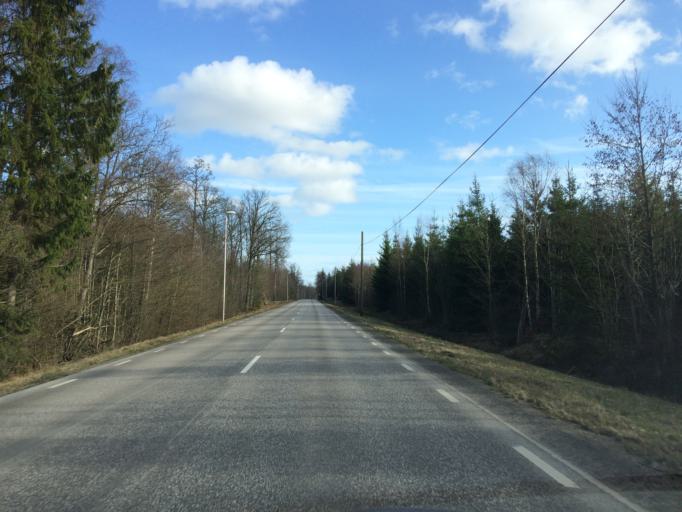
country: SE
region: Kronoberg
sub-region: Almhults Kommun
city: AElmhult
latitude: 56.5697
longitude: 14.1202
